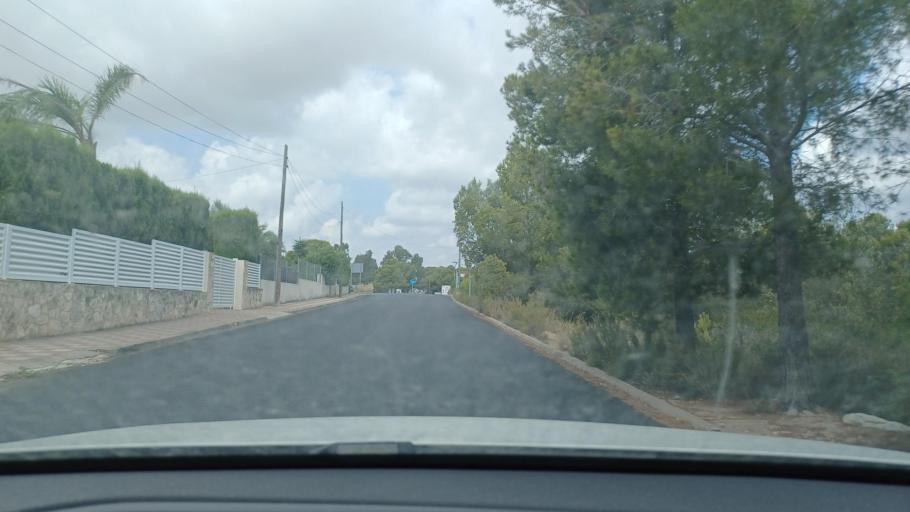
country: ES
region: Catalonia
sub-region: Provincia de Tarragona
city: l'Ametlla de Mar
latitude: 40.9077
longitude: 0.8116
